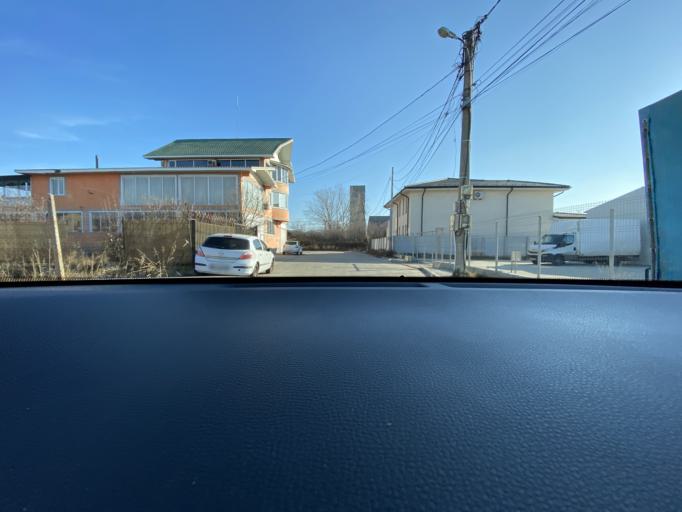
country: RO
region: Olt
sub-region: Municipiul Slatina
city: Slatina
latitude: 44.4366
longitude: 24.3737
